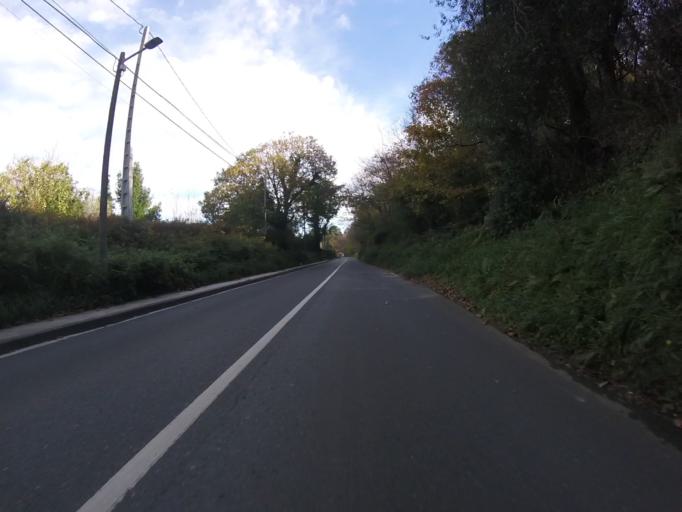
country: ES
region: Basque Country
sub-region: Provincia de Guipuzcoa
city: Lasarte
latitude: 43.3151
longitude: -2.0256
